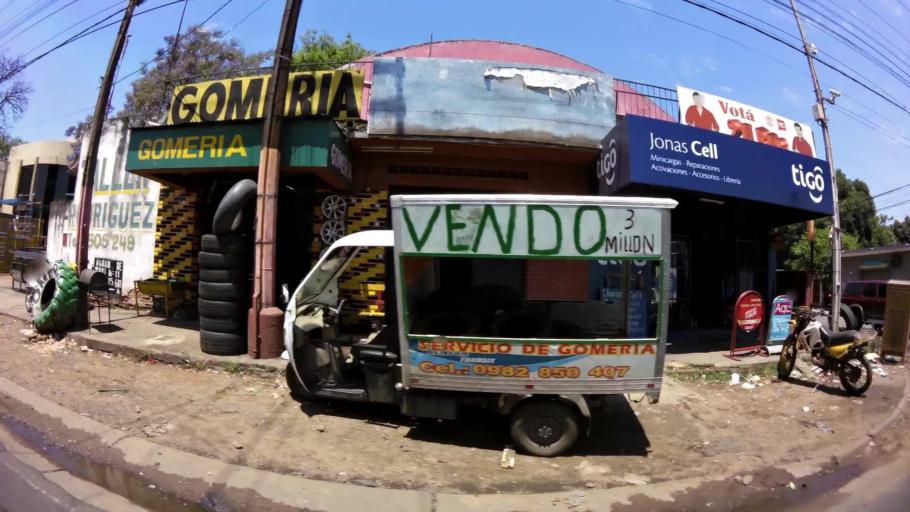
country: PY
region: Central
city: Lambare
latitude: -25.3309
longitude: -57.5741
